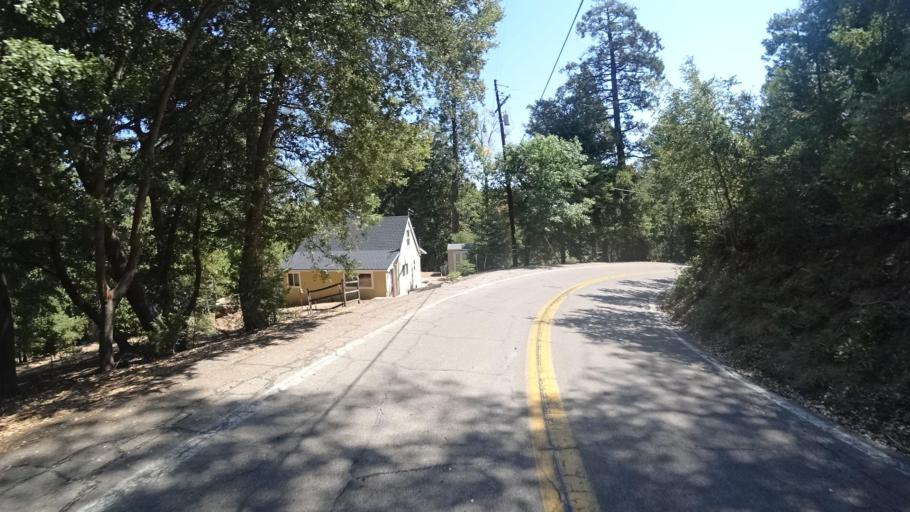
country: US
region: California
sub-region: Riverside County
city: Aguanga
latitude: 33.3225
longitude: -116.8791
